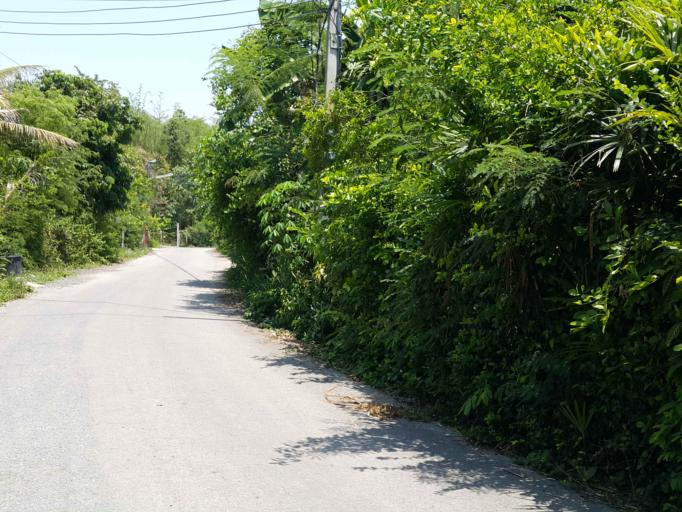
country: TH
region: Chiang Mai
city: San Sai
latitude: 18.8337
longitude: 99.1081
